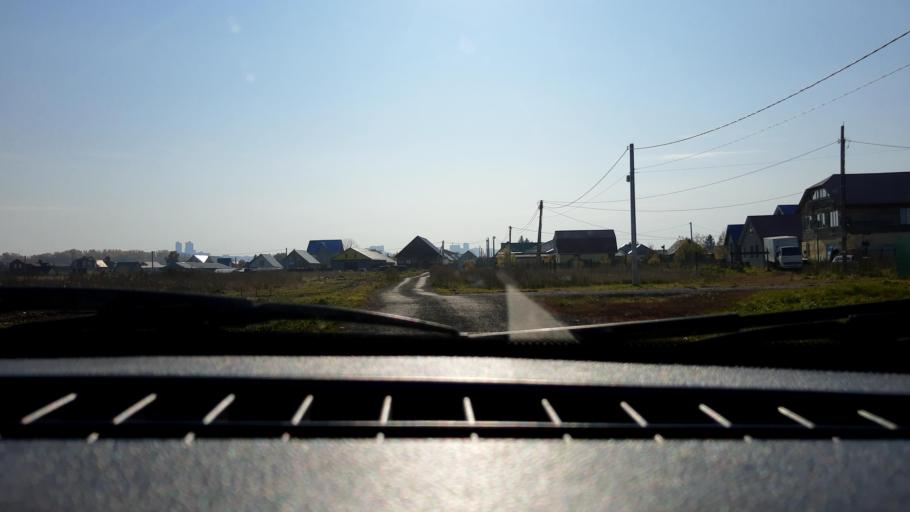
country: RU
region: Bashkortostan
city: Mikhaylovka
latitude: 54.7660
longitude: 55.9036
